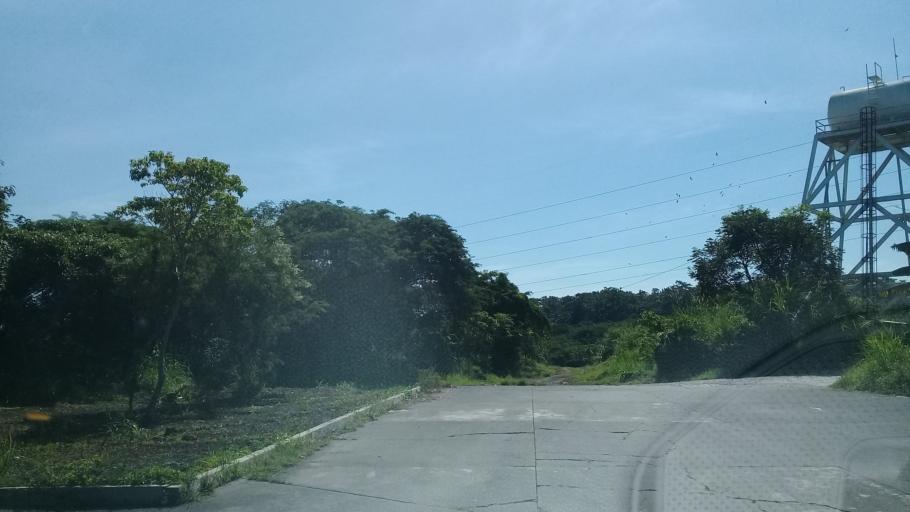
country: MX
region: Veracruz
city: Amatlan de los Reyes
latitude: 18.8577
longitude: -96.9094
